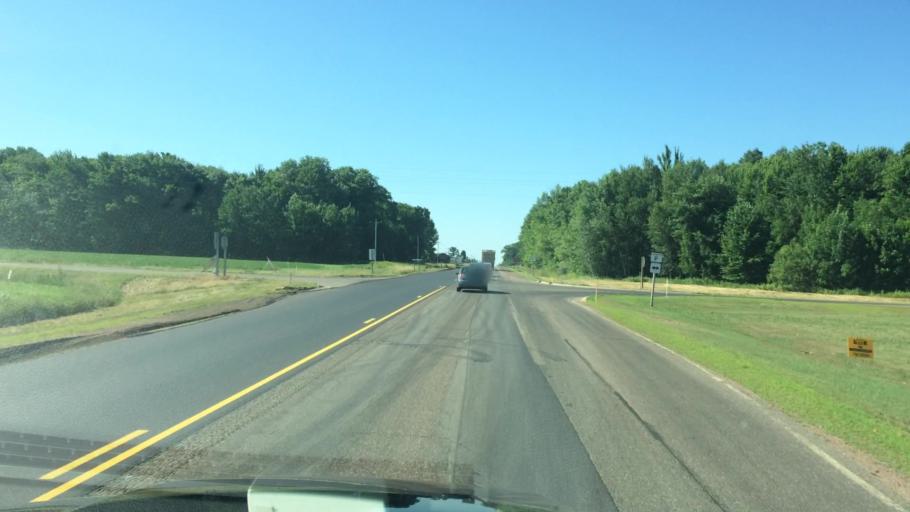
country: US
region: Wisconsin
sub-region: Marathon County
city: Stratford
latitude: 44.8593
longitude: -90.0791
